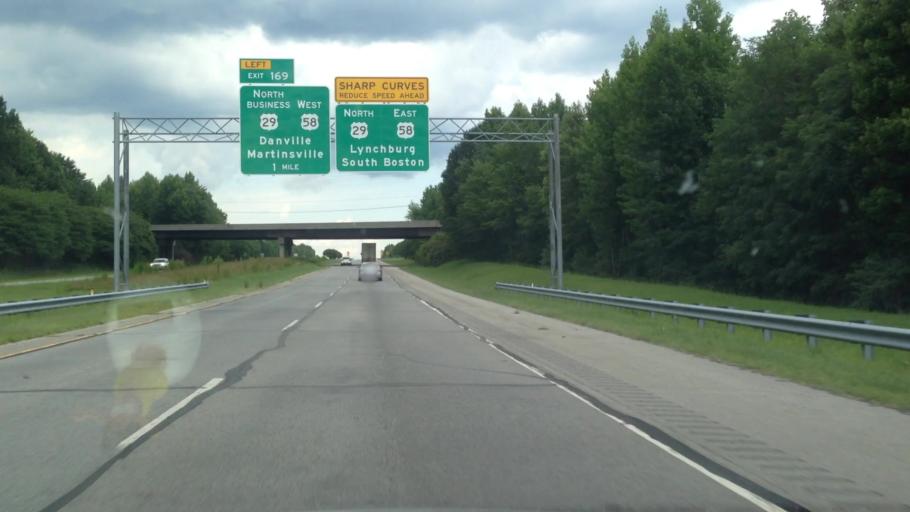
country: US
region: Virginia
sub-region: City of Danville
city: Danville
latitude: 36.5175
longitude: -79.4748
